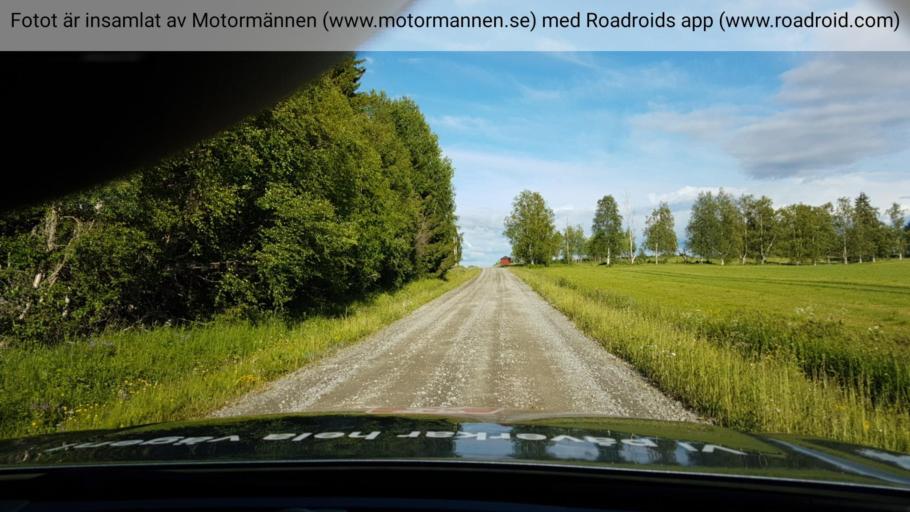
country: SE
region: Jaemtland
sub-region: Bergs Kommun
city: Hoverberg
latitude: 62.9360
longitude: 14.4181
